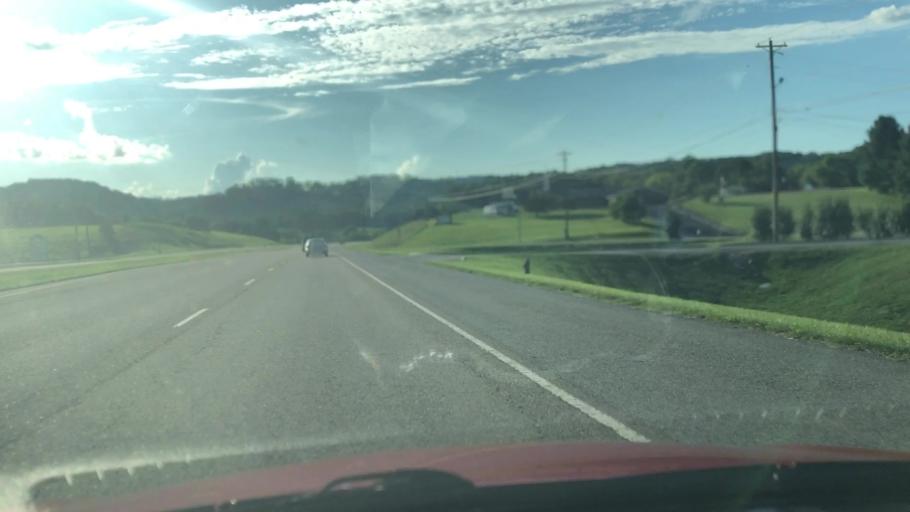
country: US
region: Tennessee
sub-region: Jefferson County
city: Dandridge
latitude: 36.0464
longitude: -83.4568
